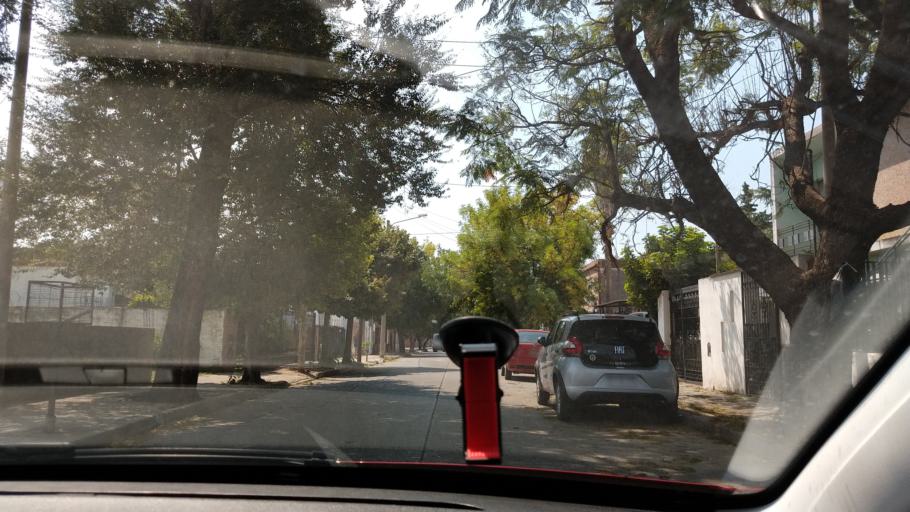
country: AR
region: Cordoba
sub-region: Departamento de Capital
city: Cordoba
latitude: -31.3901
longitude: -64.2092
